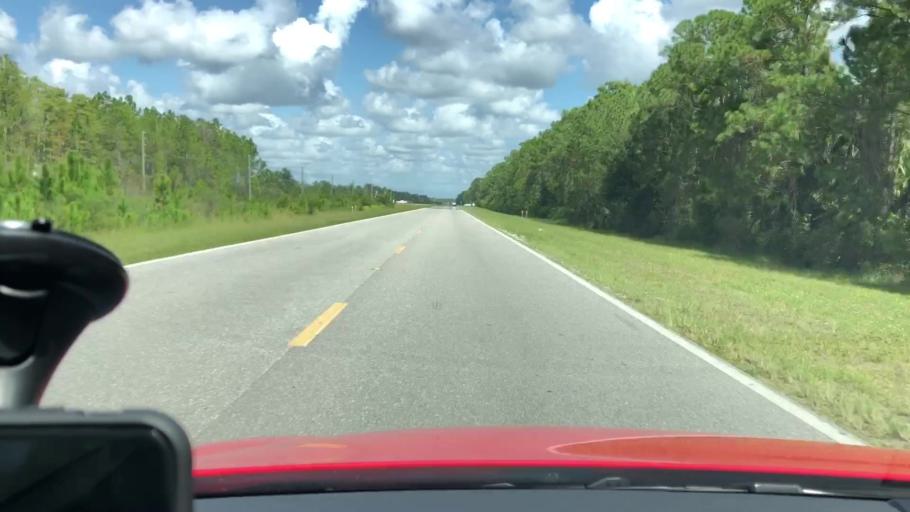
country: US
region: Florida
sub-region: Volusia County
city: Daytona Beach
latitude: 29.1865
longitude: -81.1197
